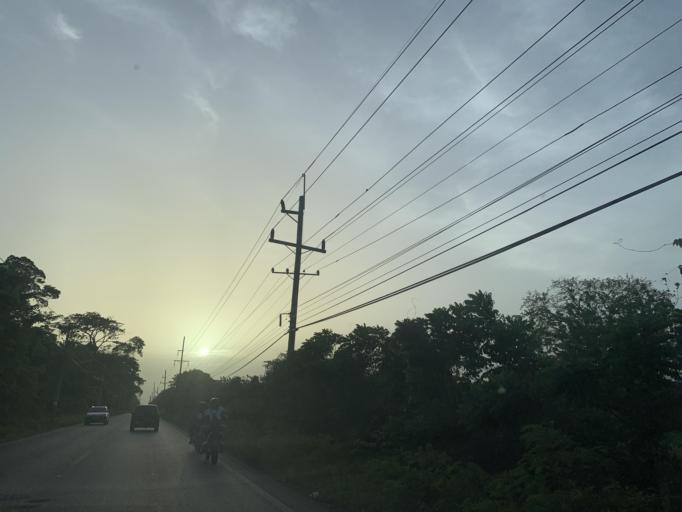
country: DO
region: Puerto Plata
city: Cabarete
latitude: 19.7759
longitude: -70.4678
